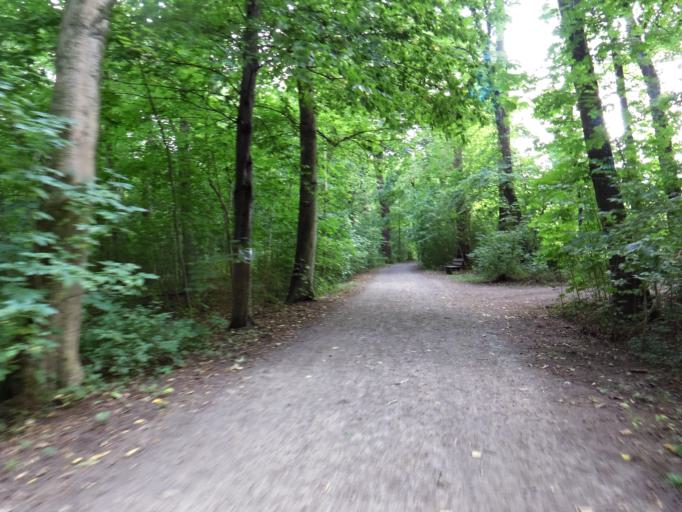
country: DE
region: Saxony
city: Leipzig
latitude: 51.3533
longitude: 12.3270
